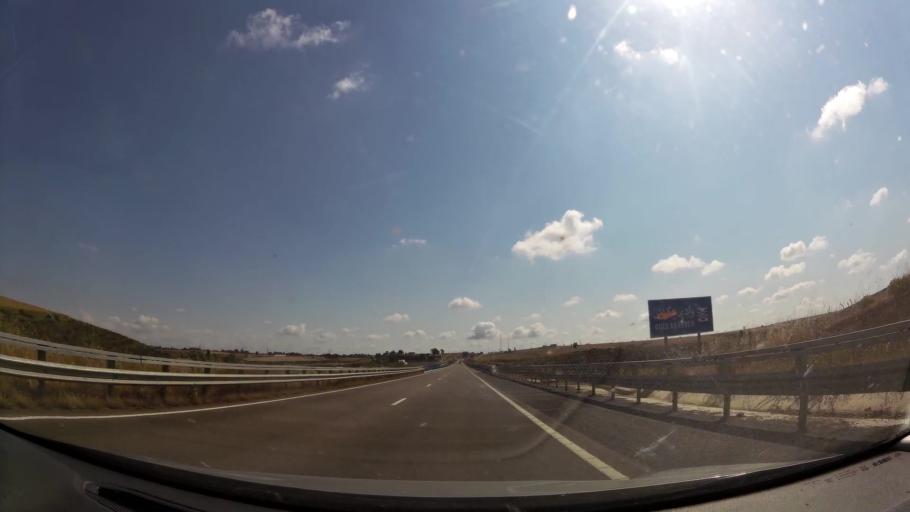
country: MA
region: Rabat-Sale-Zemmour-Zaer
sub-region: Skhirate-Temara
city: Temara
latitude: 33.8569
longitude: -6.8217
